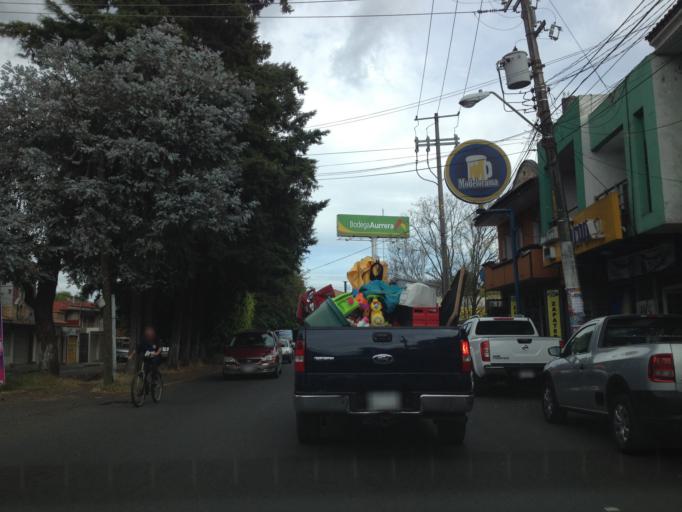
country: MX
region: Michoacan
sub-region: Uruapan
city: Uruapan
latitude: 19.4161
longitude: -102.0361
